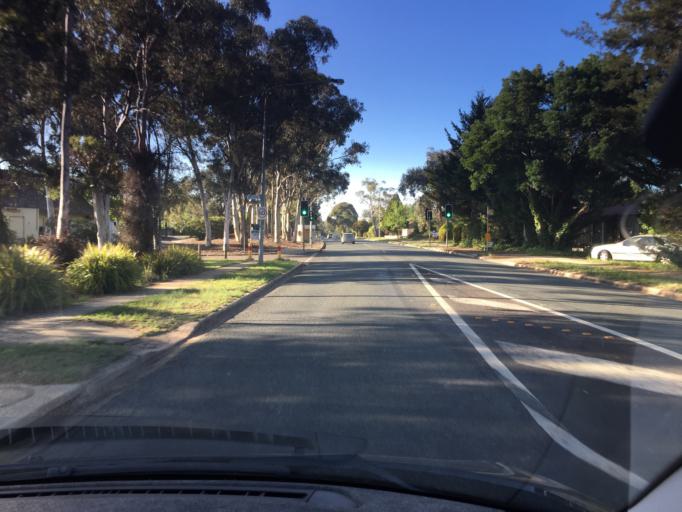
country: AU
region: Australian Capital Territory
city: Kaleen
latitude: -35.2235
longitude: 149.1110
